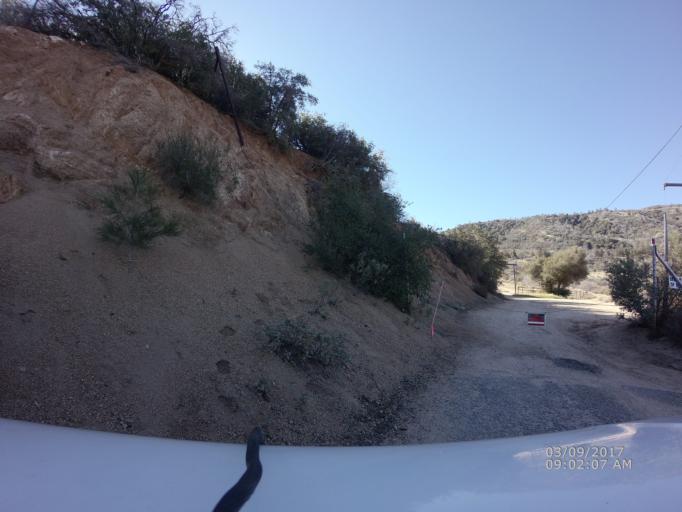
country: US
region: California
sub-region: Los Angeles County
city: Green Valley
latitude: 34.7308
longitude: -118.5996
